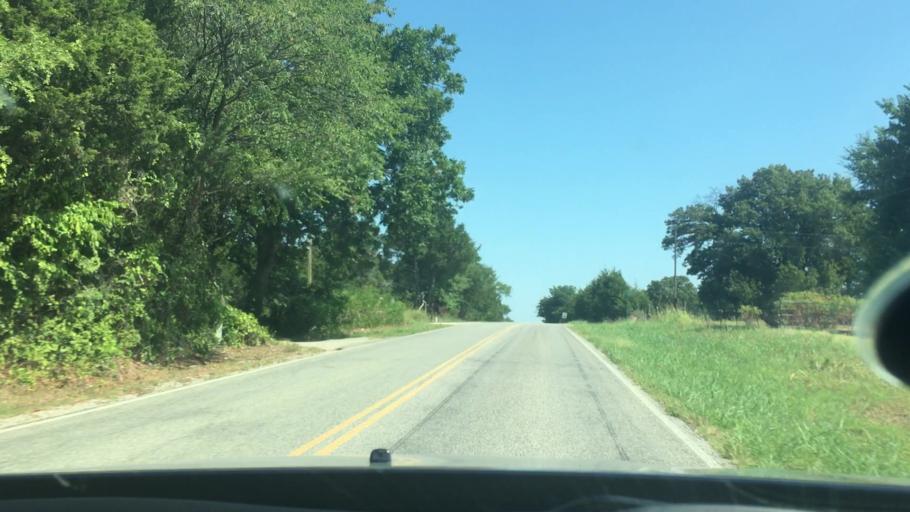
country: US
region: Oklahoma
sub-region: Johnston County
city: Tishomingo
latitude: 34.2588
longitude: -96.6186
